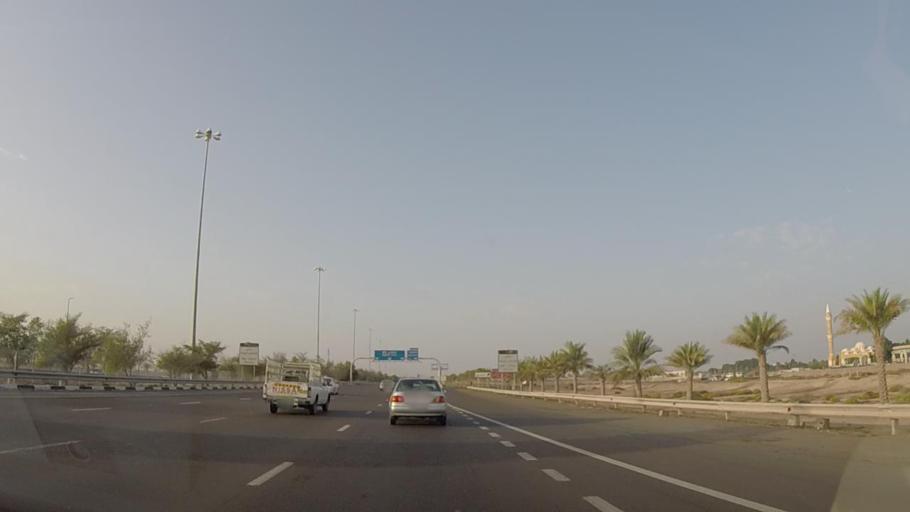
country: AE
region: Dubai
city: Dubai
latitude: 24.8679
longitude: 54.9143
